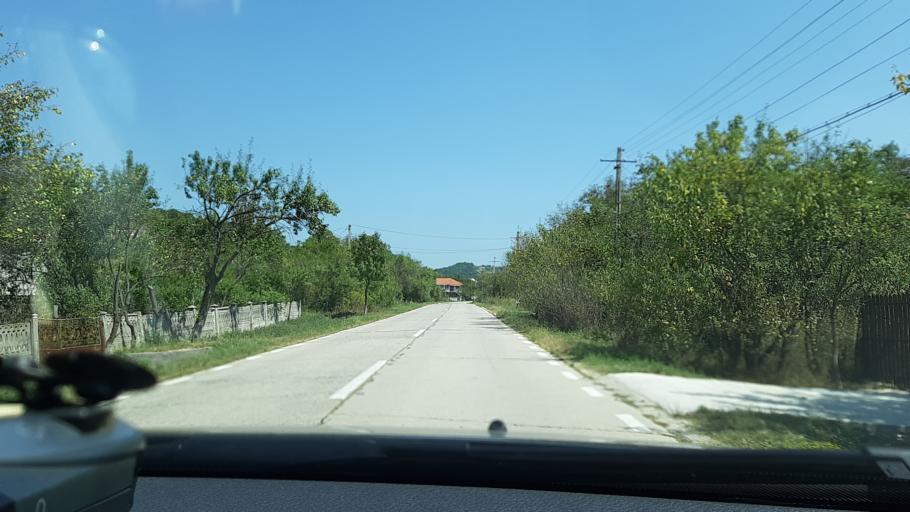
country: RO
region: Gorj
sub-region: Comuna Logresti-Mosteni
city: Logresti Mosteni
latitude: 44.9032
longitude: 23.7405
